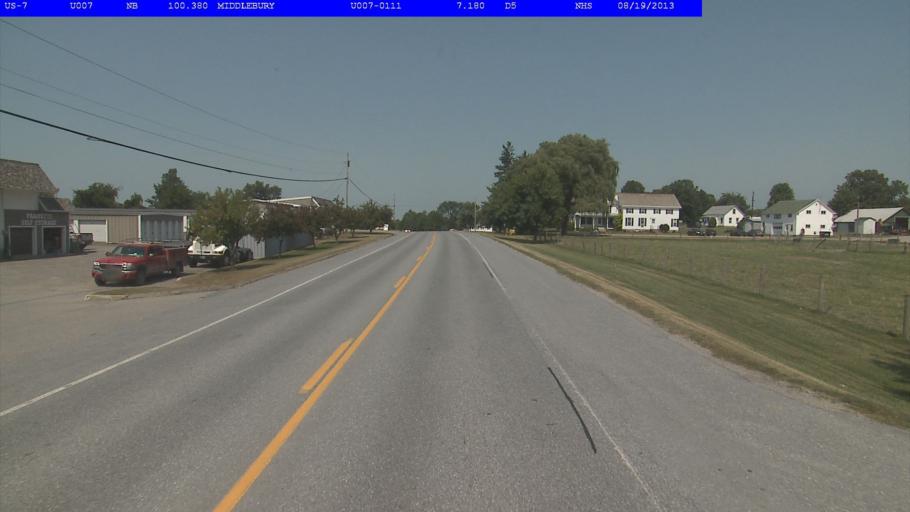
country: US
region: Vermont
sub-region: Addison County
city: Middlebury (village)
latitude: 44.0427
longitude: -73.1623
